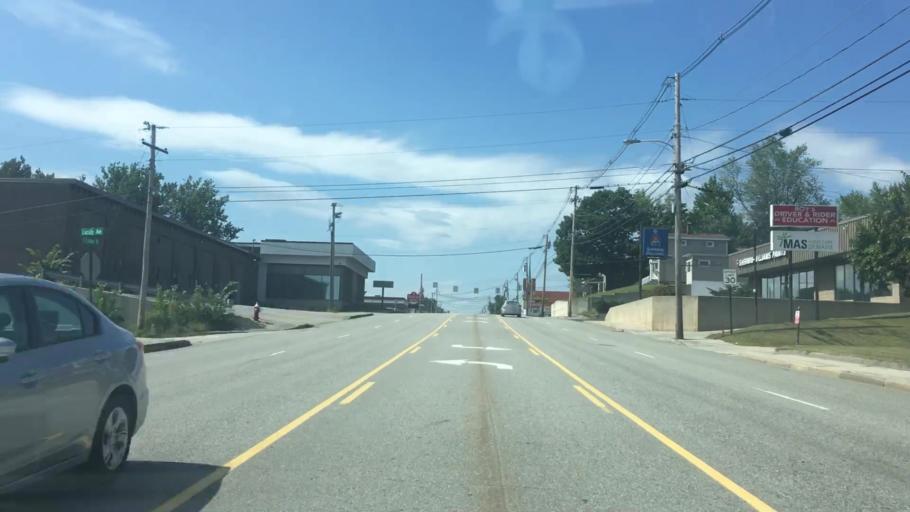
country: US
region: Maine
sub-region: Androscoggin County
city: Lewiston
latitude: 44.0779
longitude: -70.1895
